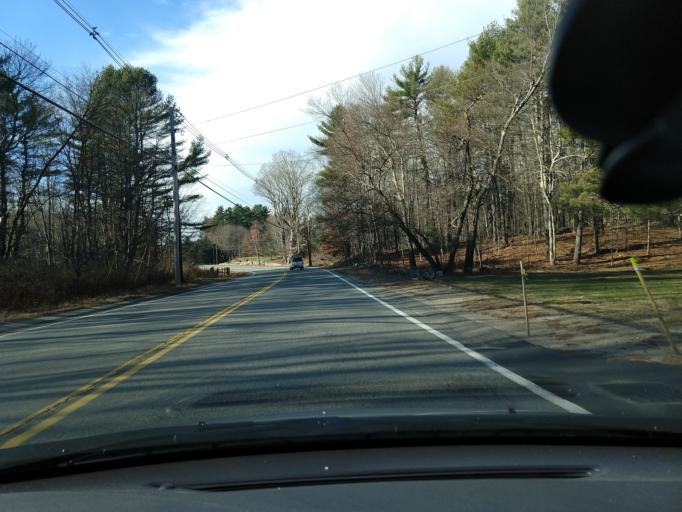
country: US
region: Massachusetts
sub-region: Middlesex County
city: Dunstable
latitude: 42.6709
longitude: -71.5085
